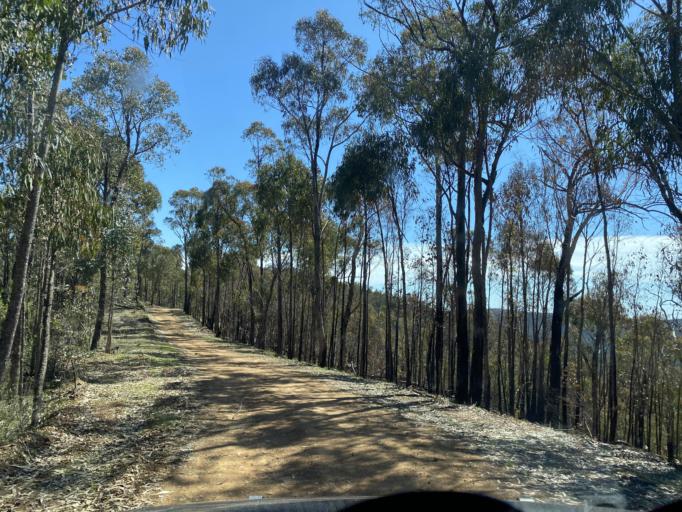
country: AU
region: Victoria
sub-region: Benalla
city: Benalla
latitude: -36.7330
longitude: 146.1830
